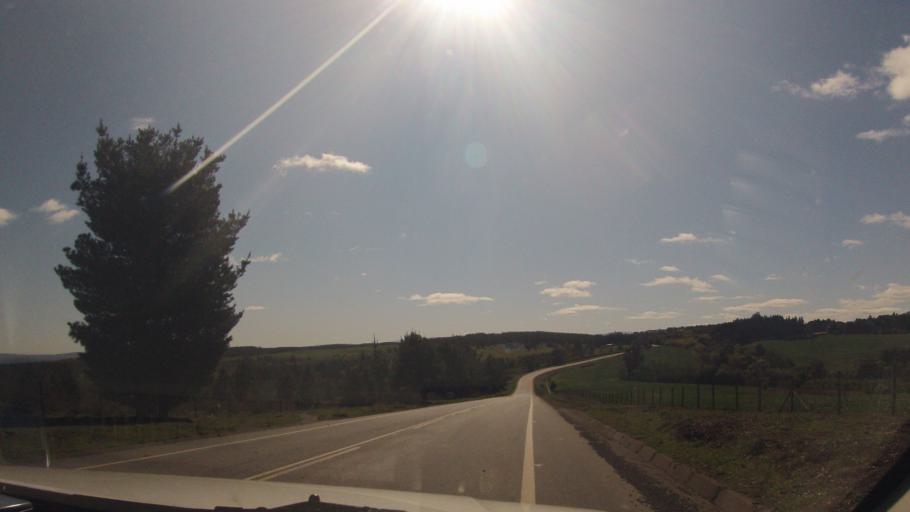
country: CL
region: Araucania
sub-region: Provincia de Malleco
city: Traiguen
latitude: -38.1956
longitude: -72.8031
